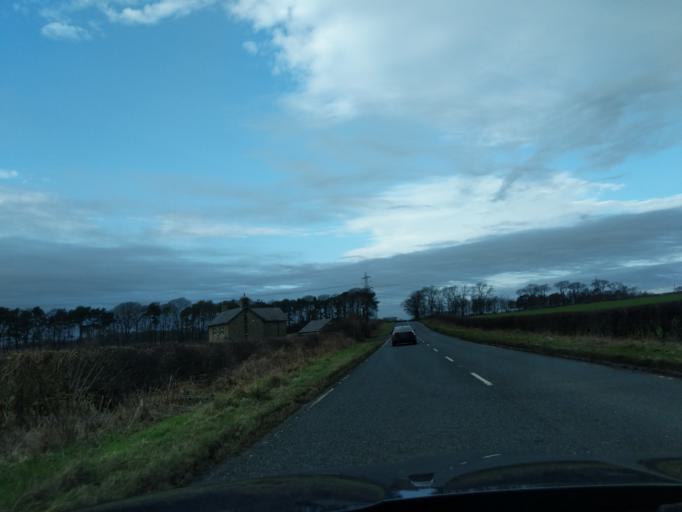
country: GB
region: England
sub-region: Northumberland
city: Meldon
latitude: 55.0993
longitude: -1.8230
